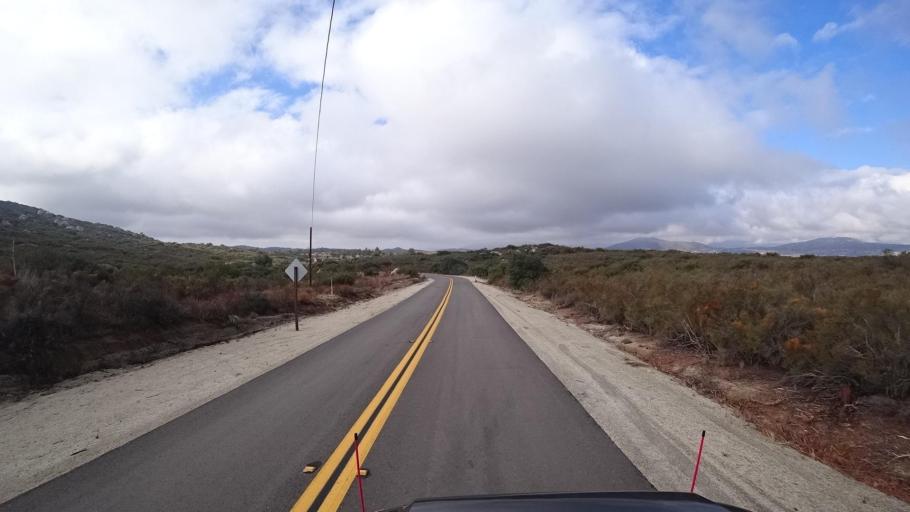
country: MX
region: Baja California
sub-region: Tecate
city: Hacienda Tecate
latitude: 32.6217
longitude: -116.5653
